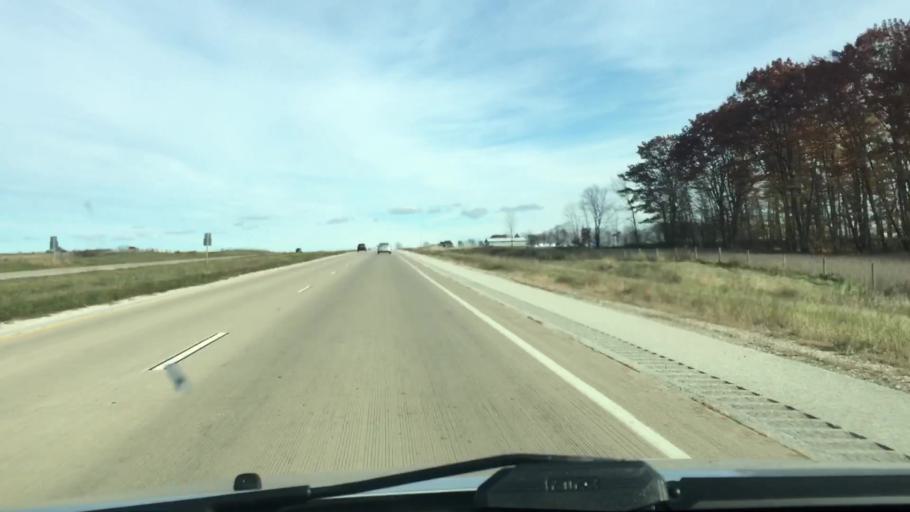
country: US
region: Wisconsin
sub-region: Kewaunee County
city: Luxemburg
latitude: 44.7166
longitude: -87.6681
